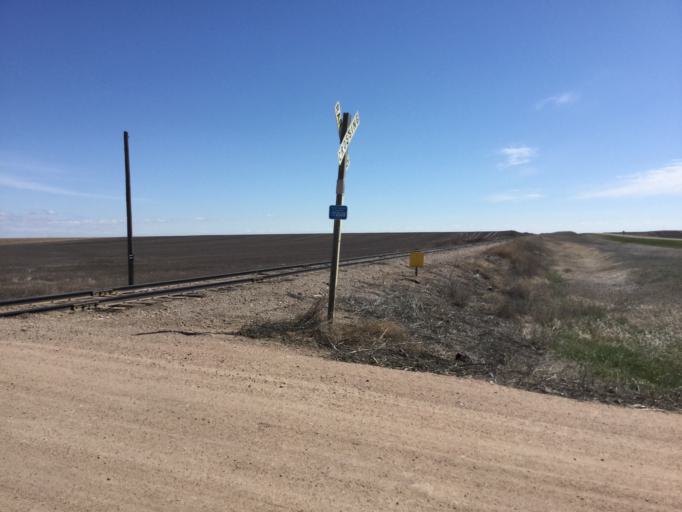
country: US
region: Kansas
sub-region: Sherman County
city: Goodland
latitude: 39.3414
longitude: -101.5214
